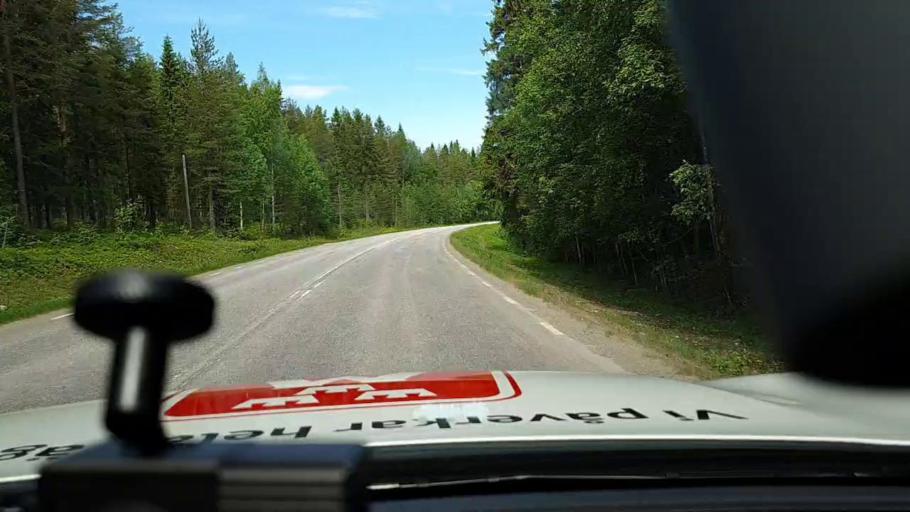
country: SE
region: Norrbotten
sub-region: Lulea Kommun
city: Gammelstad
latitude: 65.5889
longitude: 22.0038
